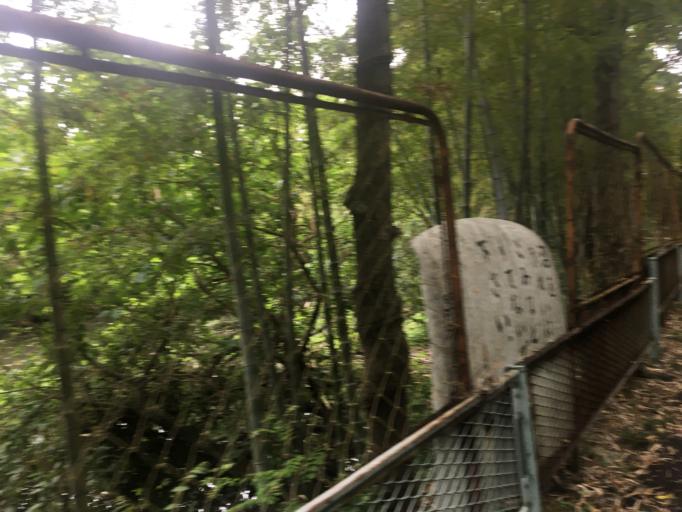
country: JP
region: Saitama
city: Sakado
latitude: 36.0317
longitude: 139.4079
